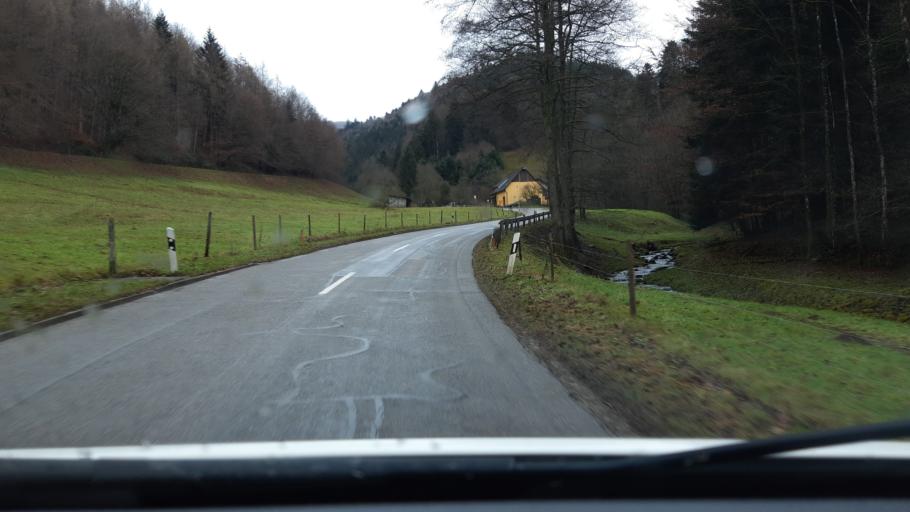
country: DE
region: Baden-Wuerttemberg
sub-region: Freiburg Region
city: Solden
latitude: 47.9112
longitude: 7.8196
